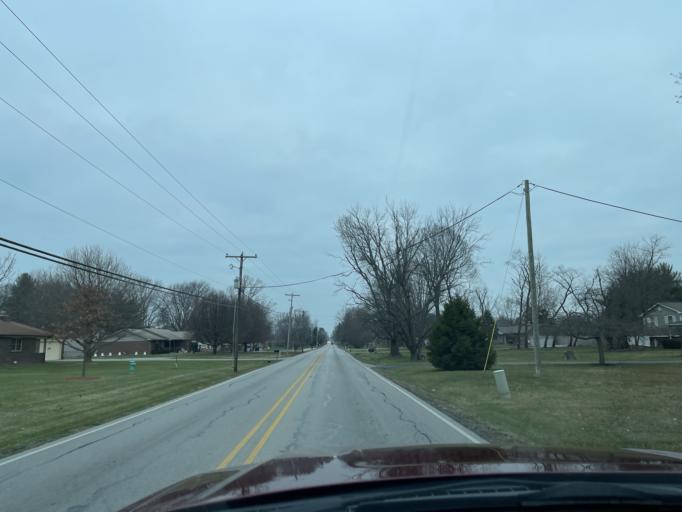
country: US
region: Indiana
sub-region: Hendricks County
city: Avon
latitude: 39.7876
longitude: -86.4002
